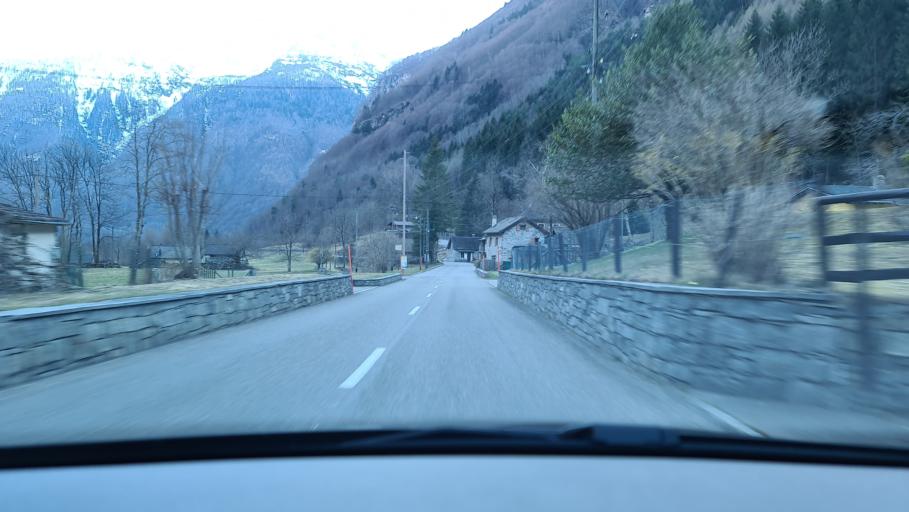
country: CH
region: Ticino
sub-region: Locarno District
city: Lavertezzo
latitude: 46.3118
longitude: 8.7994
